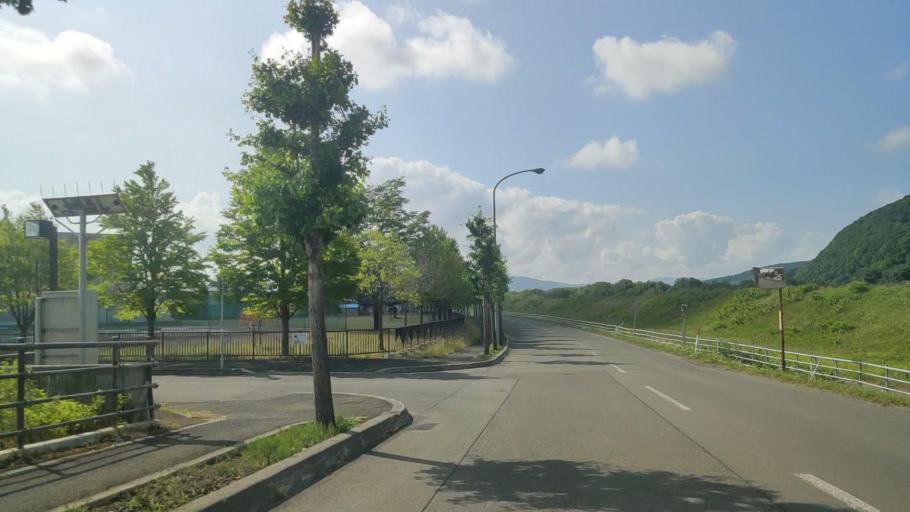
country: JP
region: Hokkaido
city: Shimo-furano
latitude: 43.3443
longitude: 142.3766
